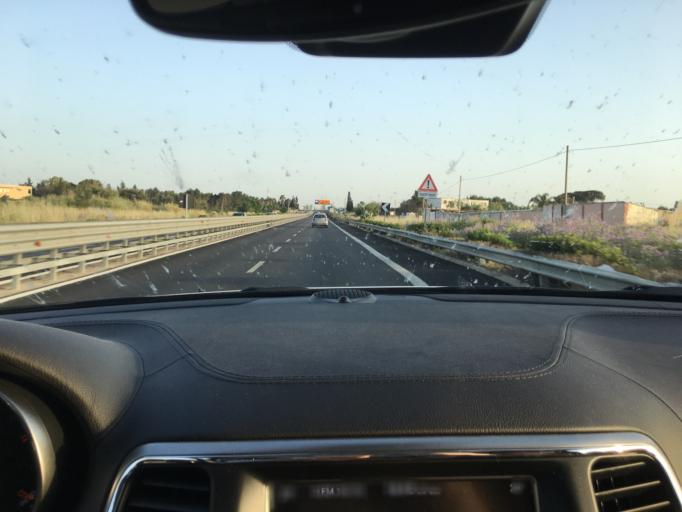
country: IT
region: Apulia
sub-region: Provincia di Lecce
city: San Pietro in Lama
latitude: 40.2966
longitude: 18.1321
